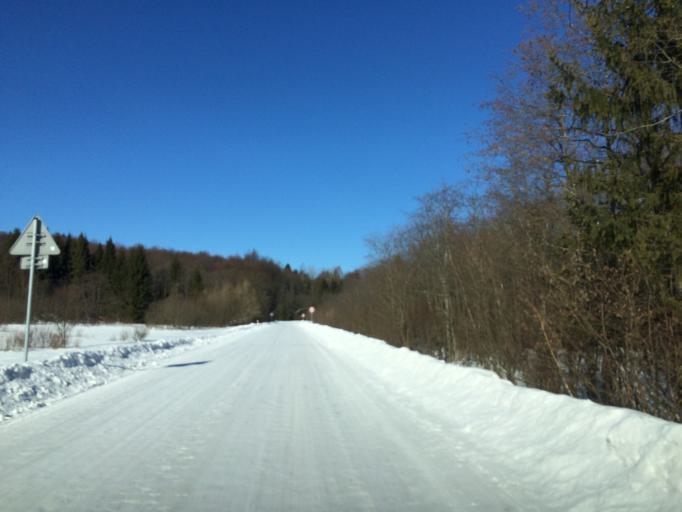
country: PL
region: Subcarpathian Voivodeship
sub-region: Powiat bieszczadzki
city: Lutowiska
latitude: 49.1040
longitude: 22.6307
